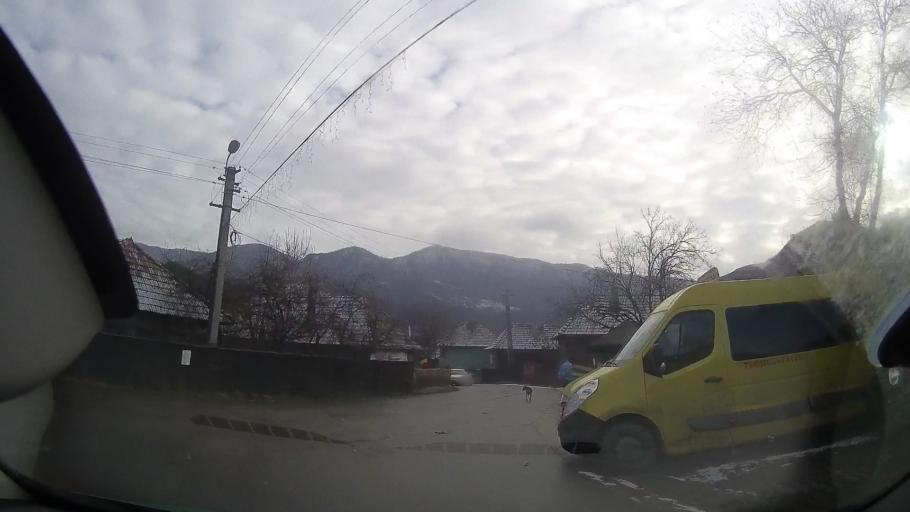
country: RO
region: Alba
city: Salciua de Sus
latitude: 46.4307
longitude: 23.4386
